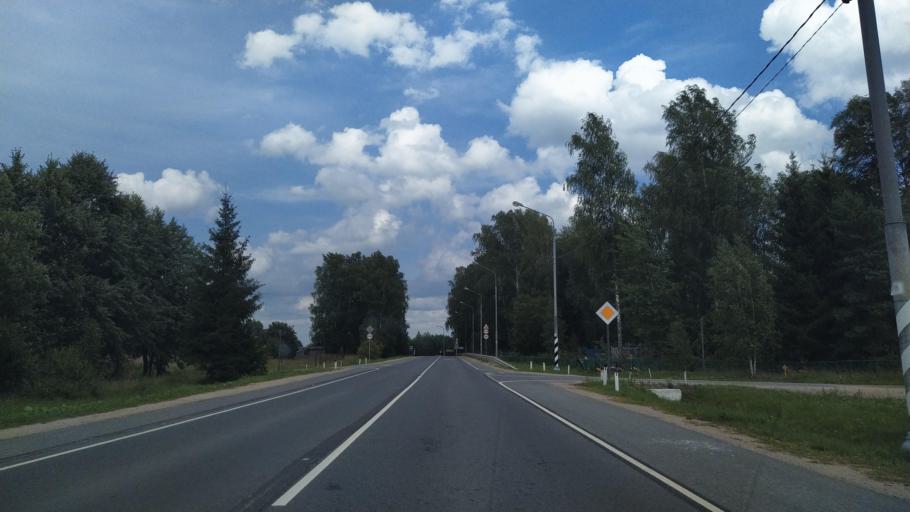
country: RU
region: Pskov
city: Dno
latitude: 58.0534
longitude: 29.9617
